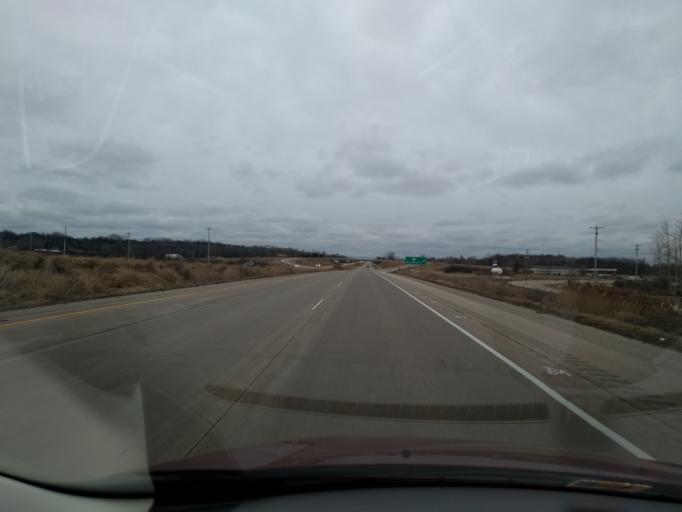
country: US
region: Wisconsin
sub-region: Winnebago County
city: Winneconne
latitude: 44.2033
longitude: -88.6815
